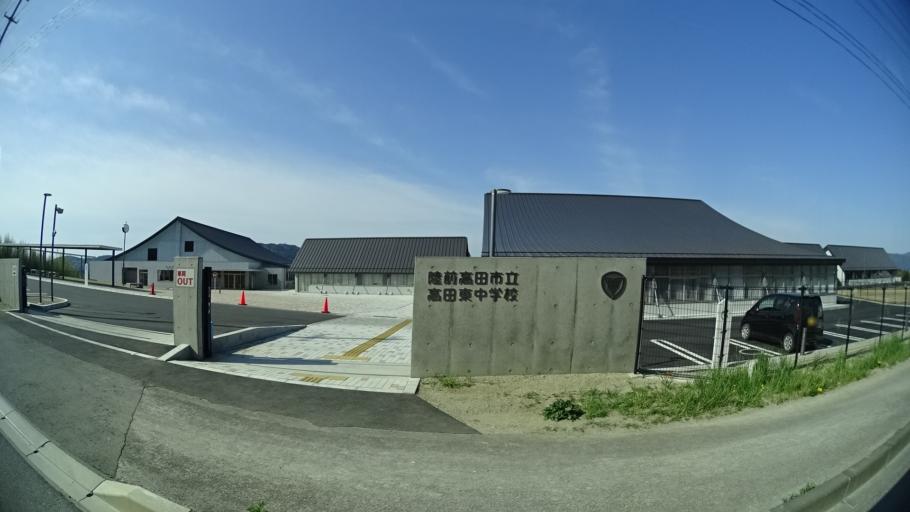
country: JP
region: Iwate
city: Ofunato
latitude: 39.0082
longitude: 141.6798
